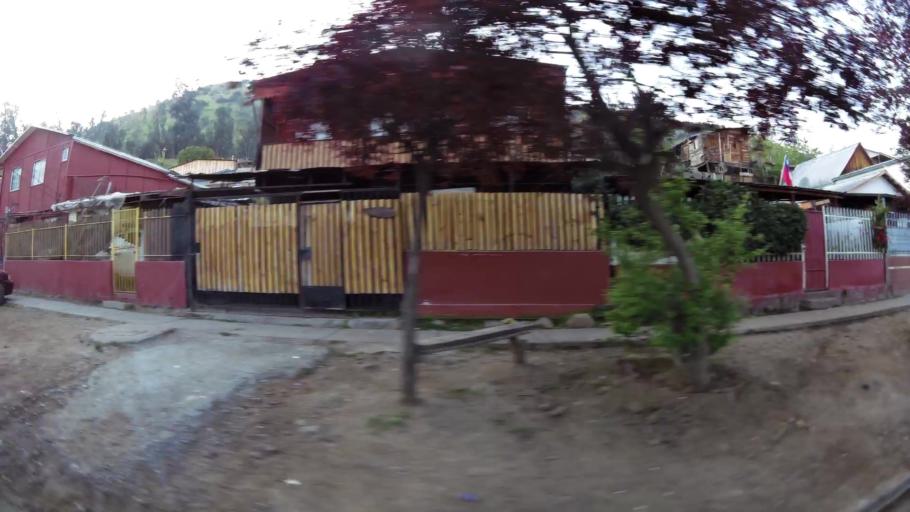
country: CL
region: Santiago Metropolitan
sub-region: Provincia de Chacabuco
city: Chicureo Abajo
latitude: -33.3680
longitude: -70.6293
